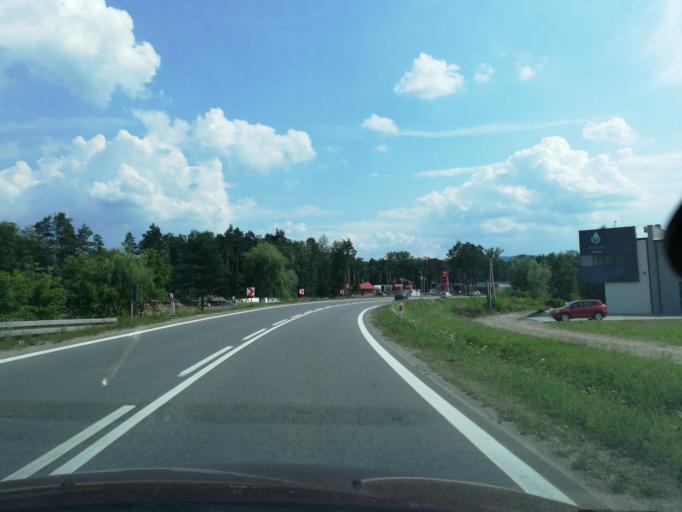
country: PL
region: Lesser Poland Voivodeship
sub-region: Powiat nowosadecki
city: Stary Sacz
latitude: 49.5697
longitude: 20.6548
